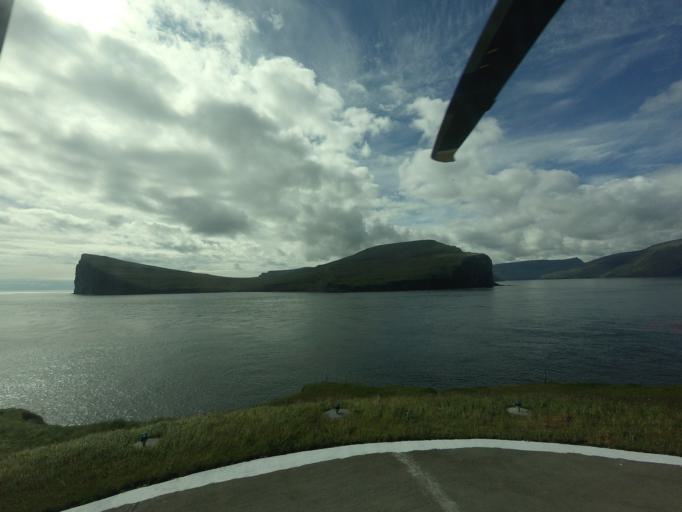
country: FO
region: Nordoyar
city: Klaksvik
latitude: 62.3172
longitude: -6.3135
